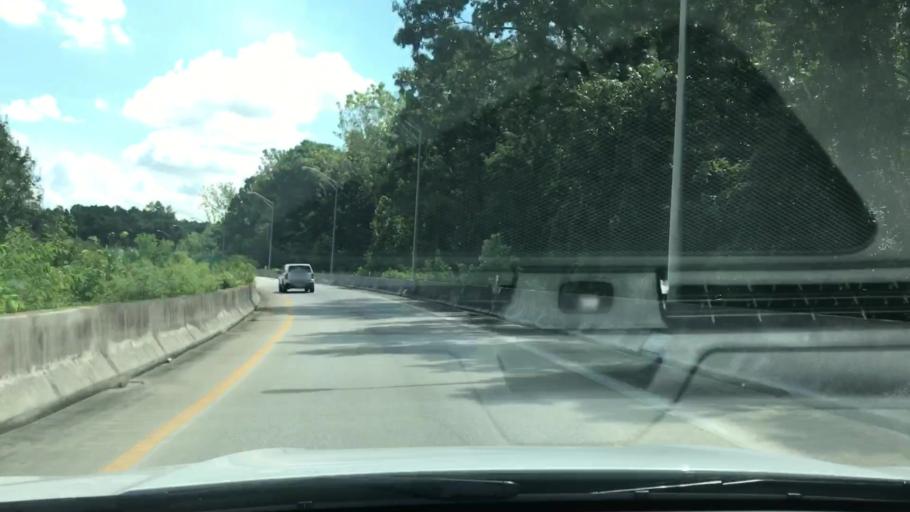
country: US
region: South Carolina
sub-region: Charleston County
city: North Charleston
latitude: 32.8932
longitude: -79.9886
